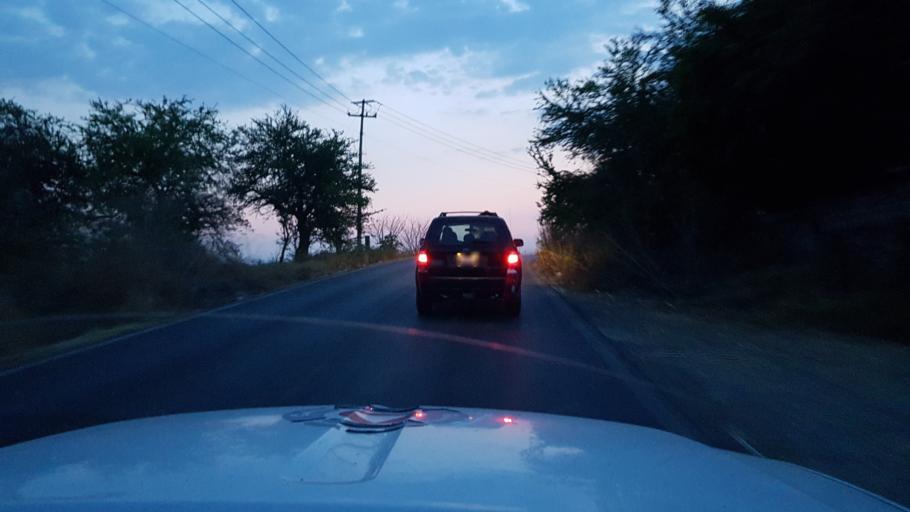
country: MX
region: Morelos
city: Tlaltizapan
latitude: 18.6876
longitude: -99.1492
